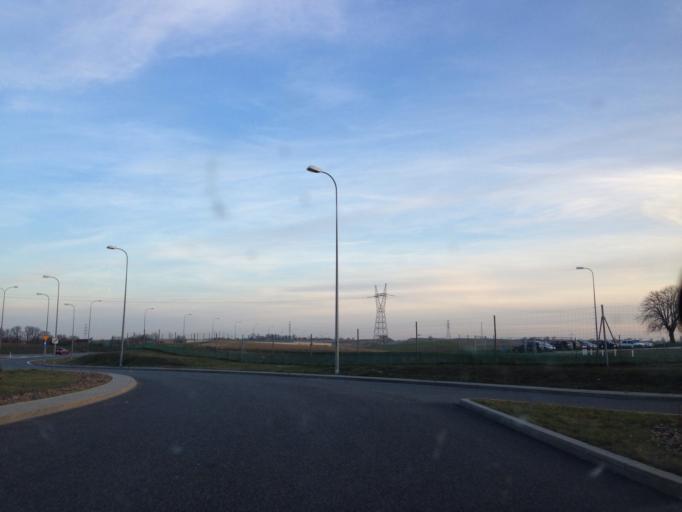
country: PL
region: Kujawsko-Pomorskie
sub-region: Powiat chelminski
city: Lisewo
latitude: 53.3403
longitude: 18.7082
